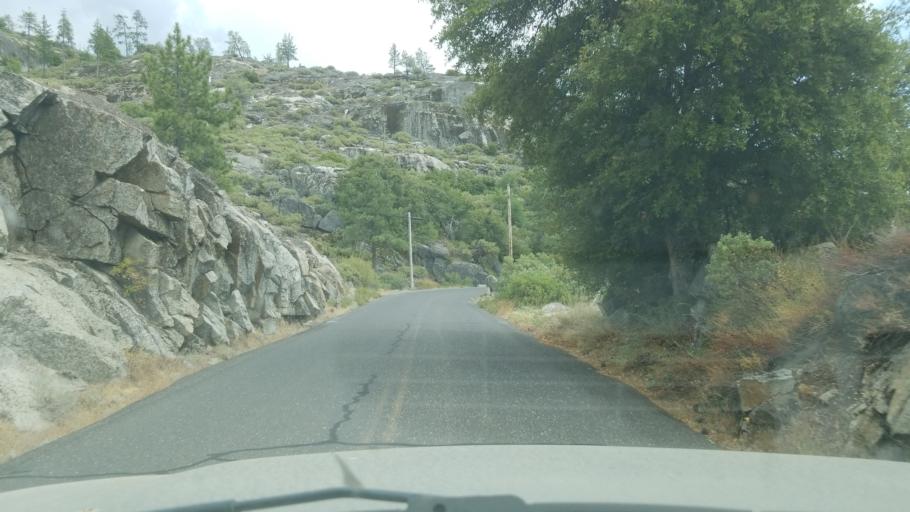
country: US
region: California
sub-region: Mariposa County
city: Yosemite Valley
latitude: 37.9002
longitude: -119.8357
